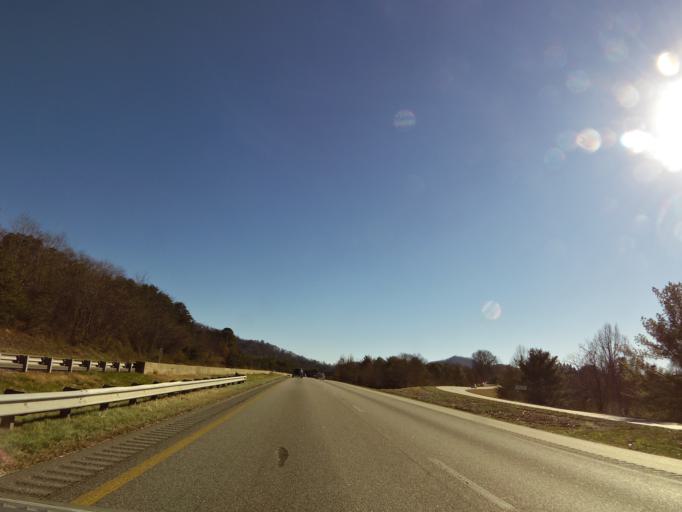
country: US
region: North Carolina
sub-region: Haywood County
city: Canton
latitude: 35.5536
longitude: -82.8223
